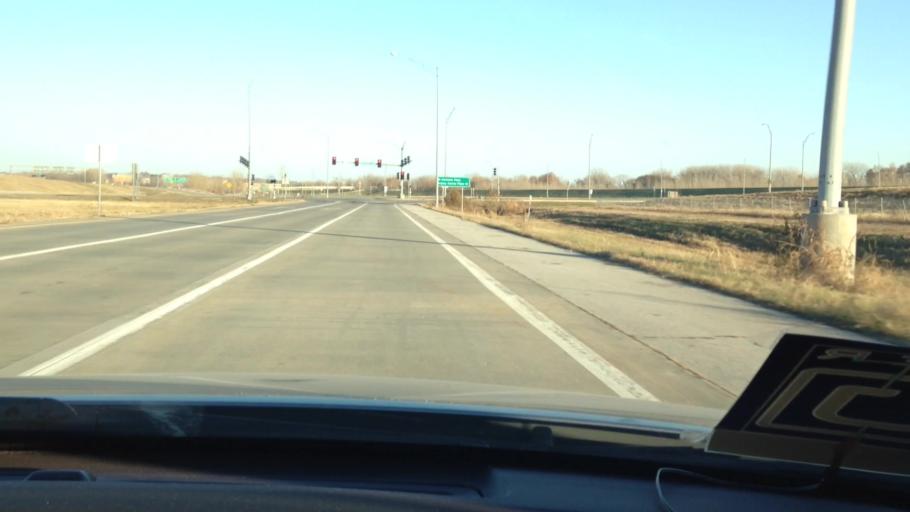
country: US
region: Missouri
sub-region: Platte County
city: Riverside
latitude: 39.1591
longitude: -94.6432
